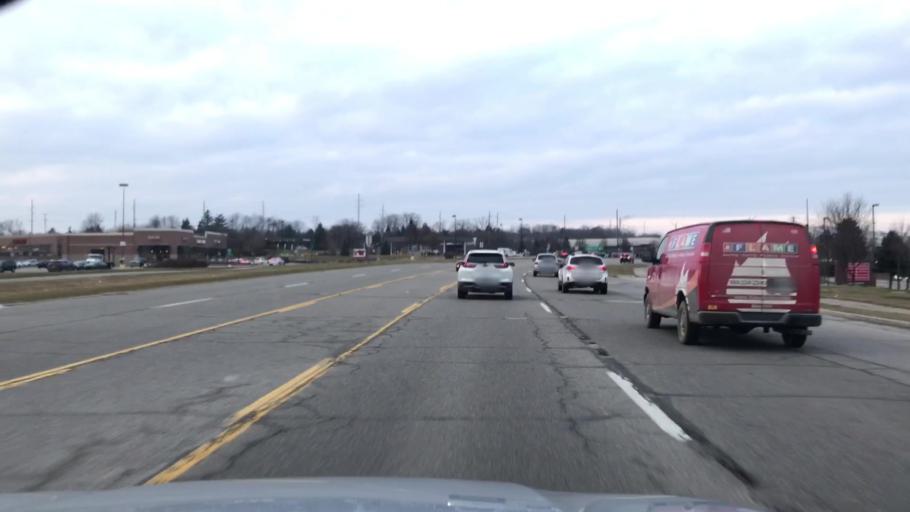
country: US
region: Michigan
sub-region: Wayne County
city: Northville
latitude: 42.4365
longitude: -83.4349
